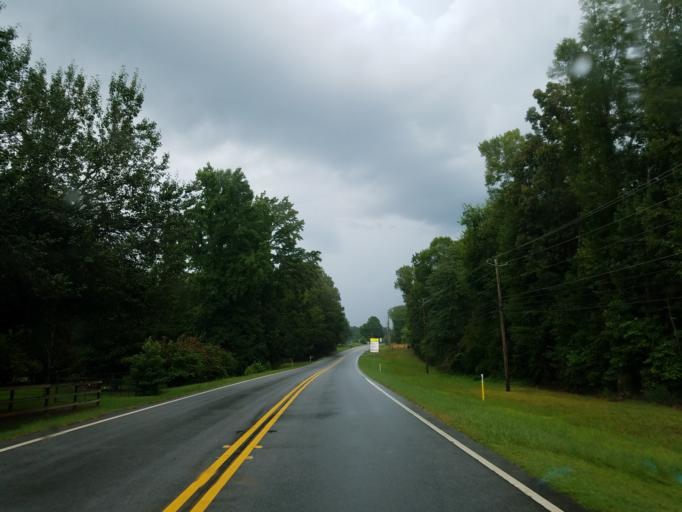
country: US
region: Georgia
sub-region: Floyd County
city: Shannon
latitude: 34.3863
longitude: -85.1721
